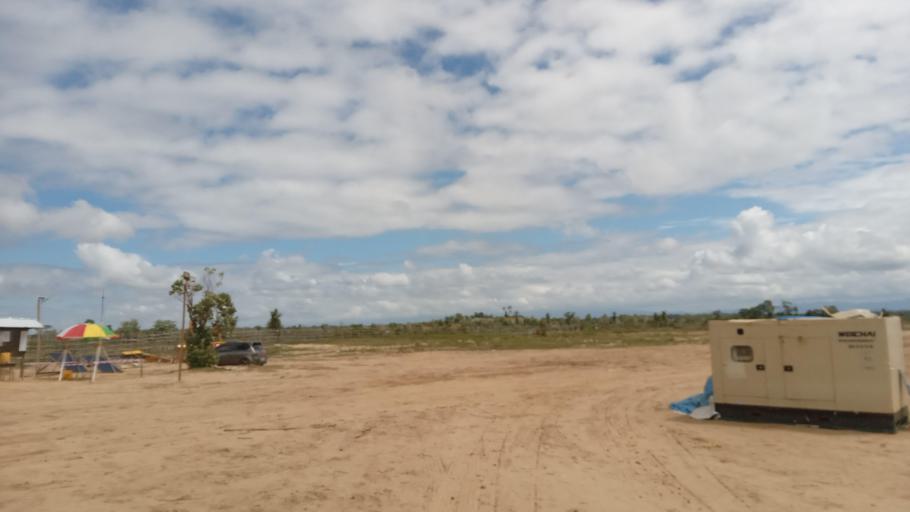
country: MG
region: Atsimo-Atsinanana
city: Vohipaho
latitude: -23.8125
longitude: 47.5502
